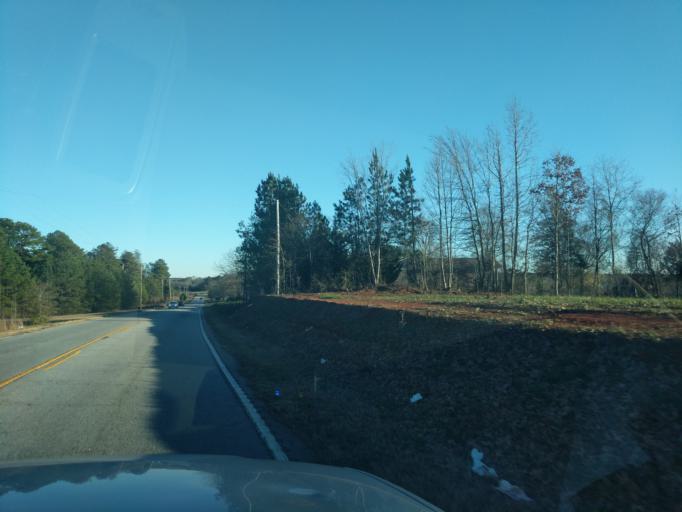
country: US
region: South Carolina
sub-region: Oconee County
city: Westminster
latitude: 34.6481
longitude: -83.0745
